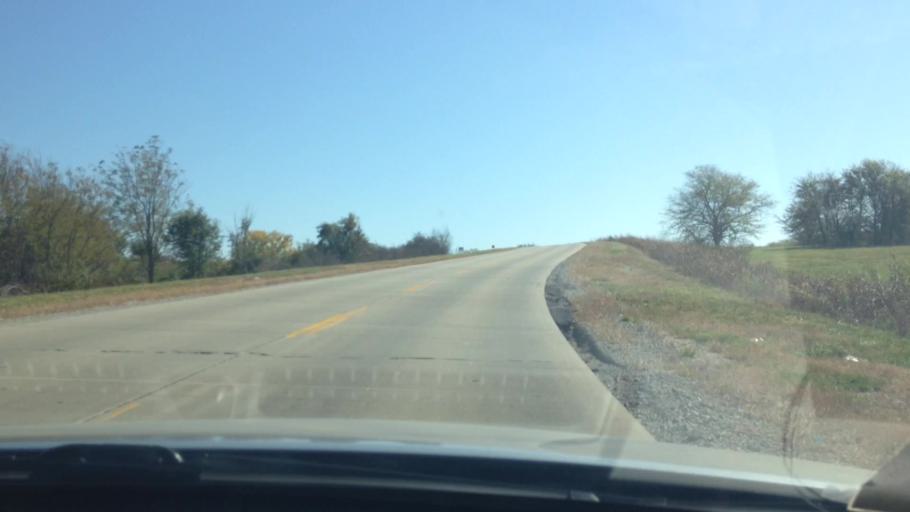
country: US
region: Missouri
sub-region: Platte County
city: Platte City
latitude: 39.3388
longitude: -94.7349
